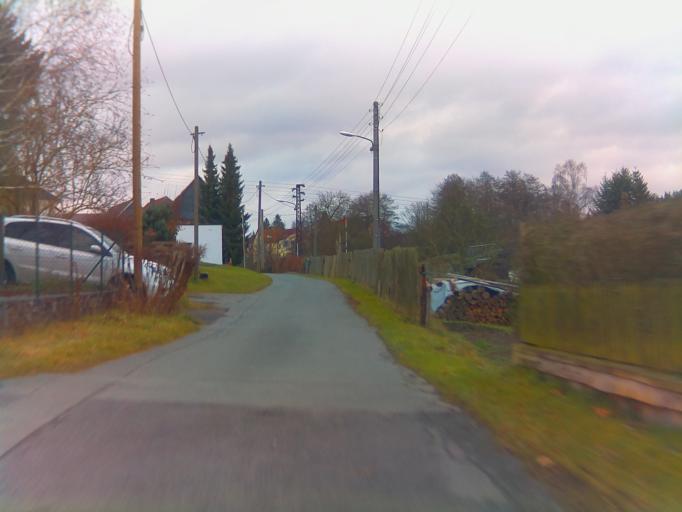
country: DE
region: Thuringia
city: Hummelshain
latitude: 50.7660
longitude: 11.6230
